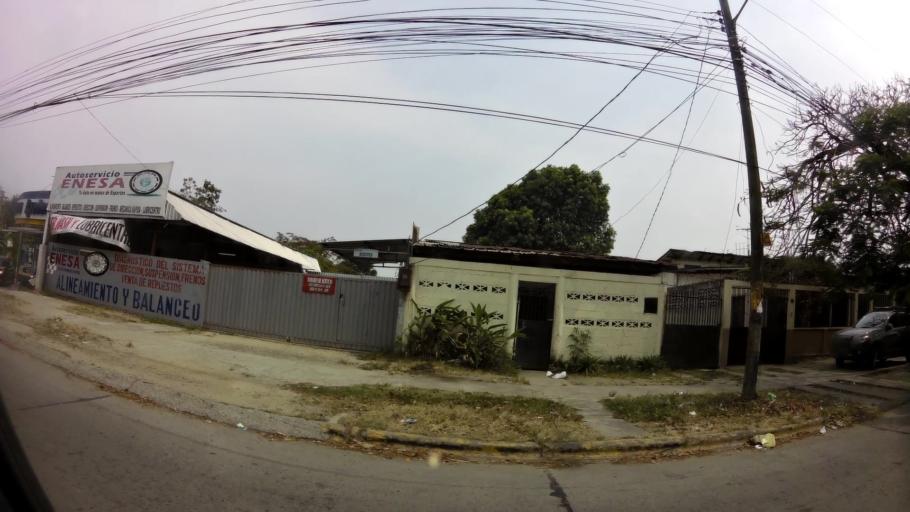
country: HN
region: Cortes
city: San Pedro Sula
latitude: 15.4898
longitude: -88.0198
